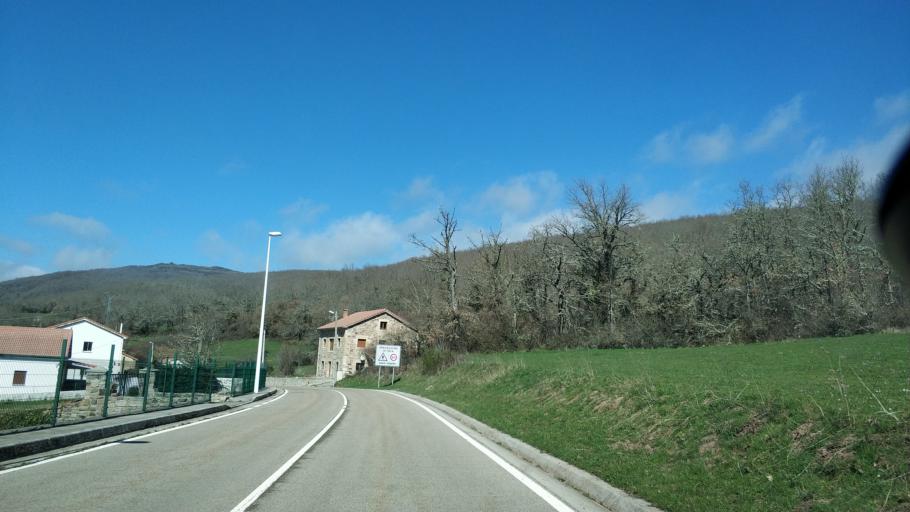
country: ES
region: Cantabria
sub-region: Provincia de Cantabria
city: Mataporquera
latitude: 42.9095
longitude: -4.0713
